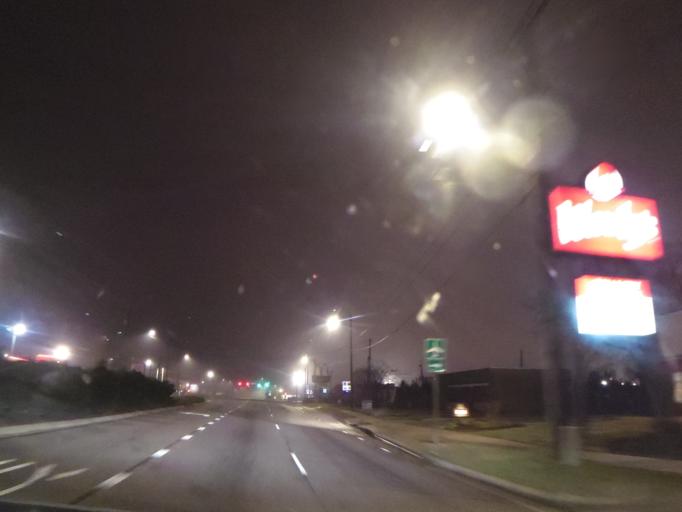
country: US
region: North Carolina
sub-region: Cumberland County
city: Fayetteville
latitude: 35.0535
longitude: -78.8663
